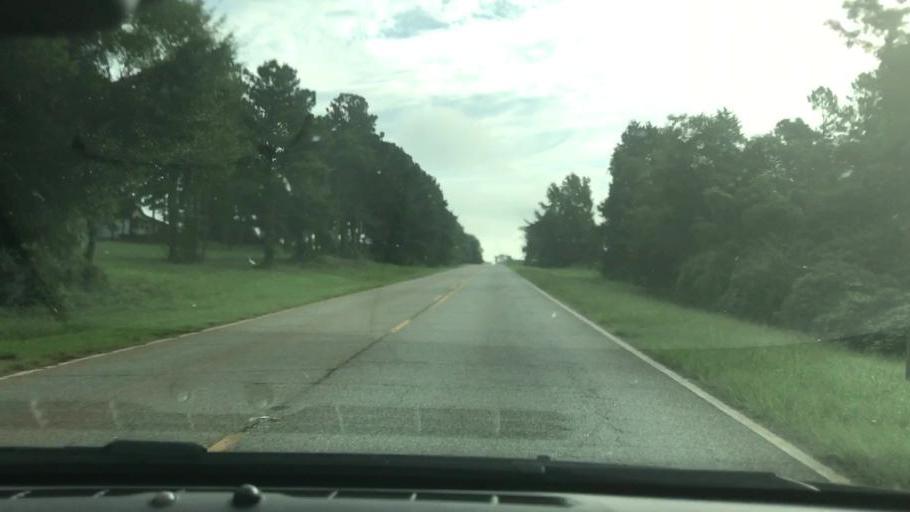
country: US
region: Georgia
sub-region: Quitman County
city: Georgetown
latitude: 31.8996
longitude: -85.0479
